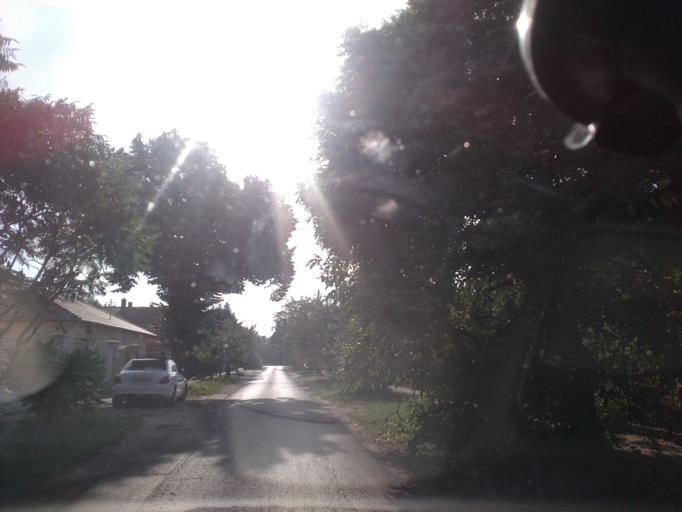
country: HU
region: Pest
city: Gyal
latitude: 47.4241
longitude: 19.2155
